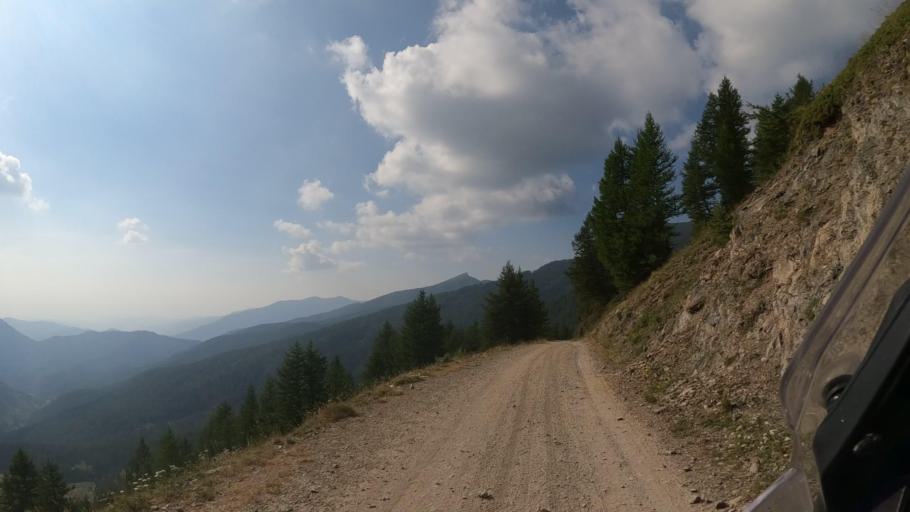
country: IT
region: Piedmont
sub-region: Provincia di Cuneo
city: Briga Alta
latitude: 44.1416
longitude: 7.6770
